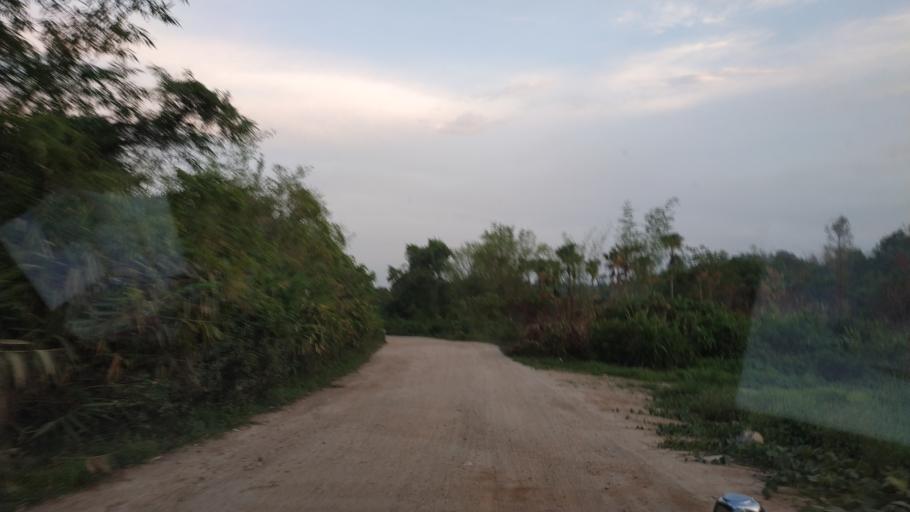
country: MM
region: Mon
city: Kyaikto
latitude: 17.4299
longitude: 97.0426
